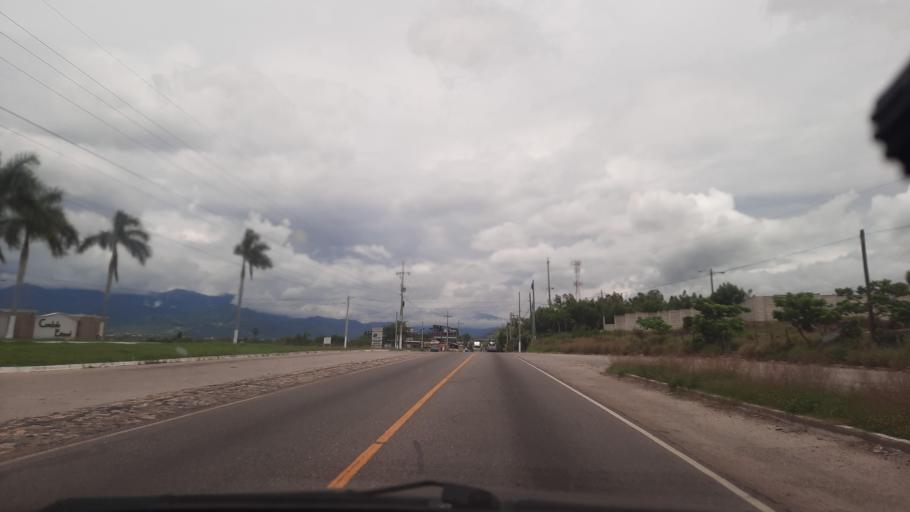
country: GT
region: Zacapa
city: Estanzuela
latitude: 15.0052
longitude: -89.5719
